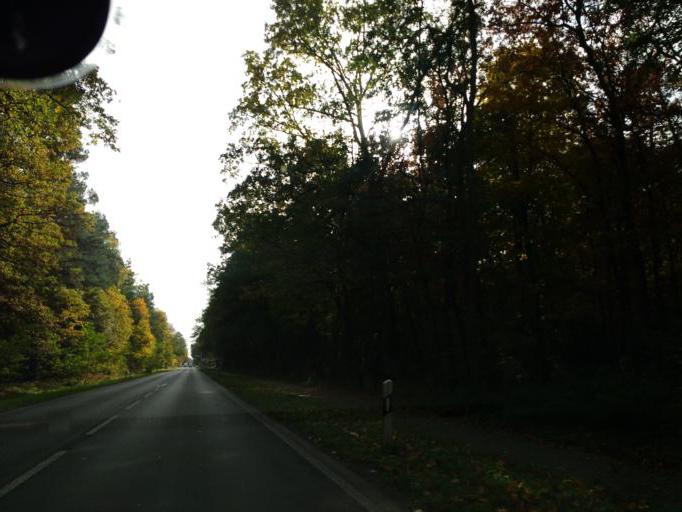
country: DE
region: Brandenburg
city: Grunheide
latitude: 52.4096
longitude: 13.8249
